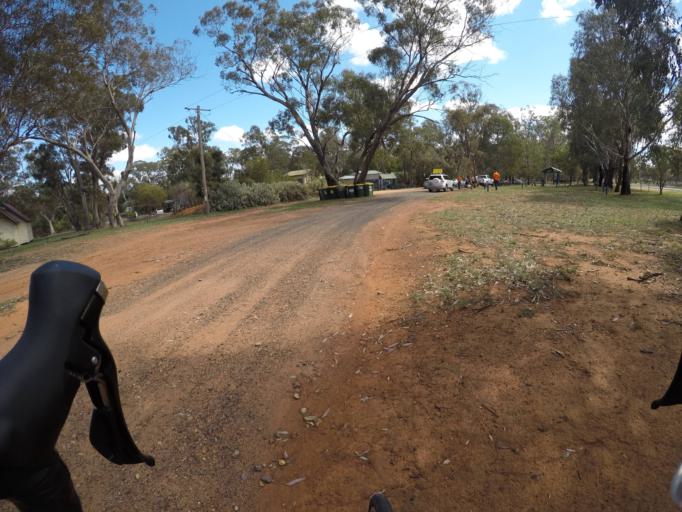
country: AU
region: New South Wales
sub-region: Dubbo Municipality
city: Dubbo
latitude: -32.4887
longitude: 148.5555
